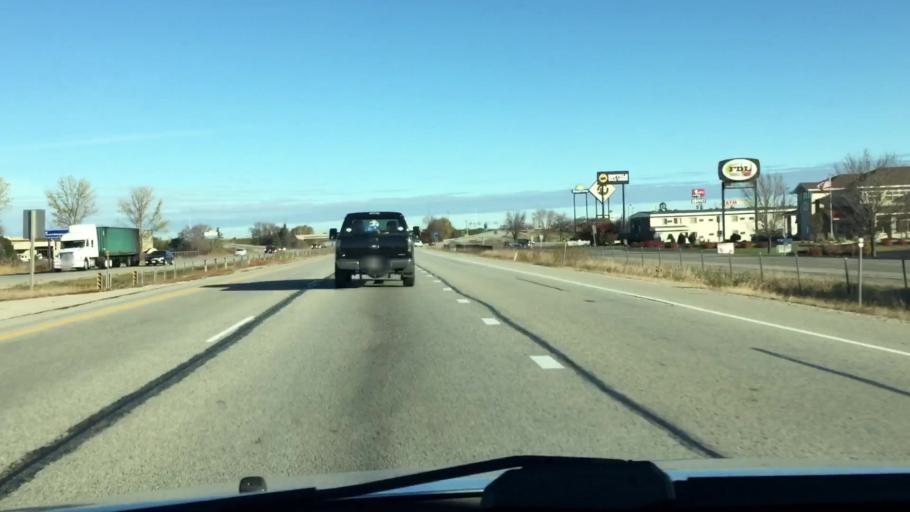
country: US
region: Wisconsin
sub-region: Fond du Lac County
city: North Fond du Lac
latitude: 43.7797
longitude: -88.4823
